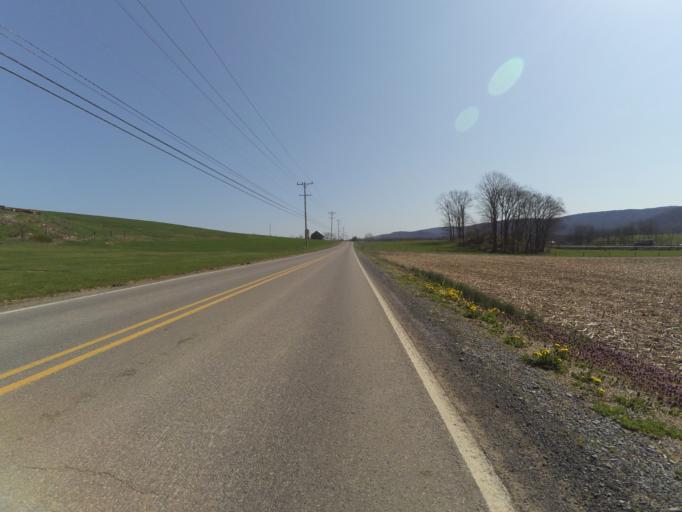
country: US
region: Pennsylvania
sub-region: Centre County
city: Zion
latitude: 40.9888
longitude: -77.5725
